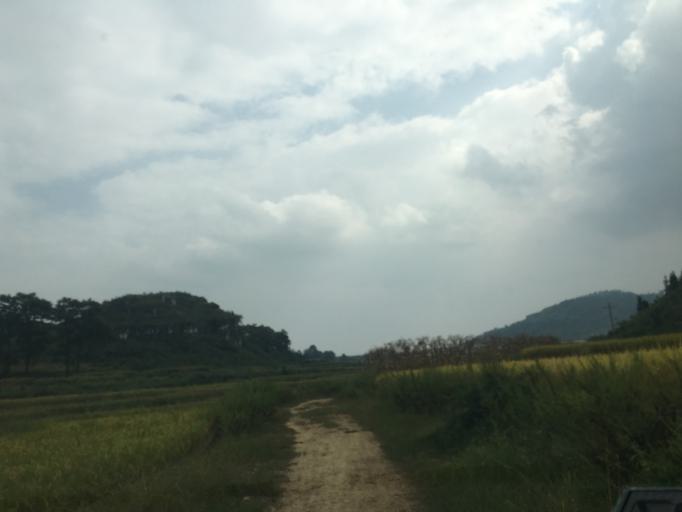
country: CN
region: Guangxi Zhuangzu Zizhiqu
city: Xinzhou
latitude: 25.4903
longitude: 105.6516
